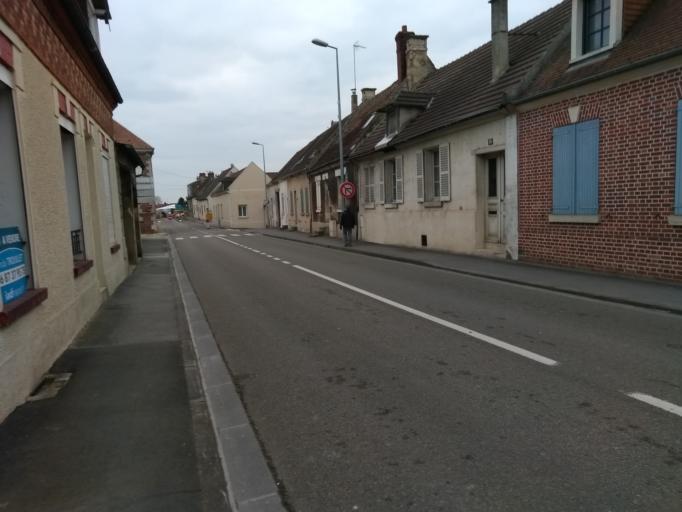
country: FR
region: Picardie
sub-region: Departement de l'Oise
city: Choisy-au-Bac
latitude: 49.4374
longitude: 2.8773
